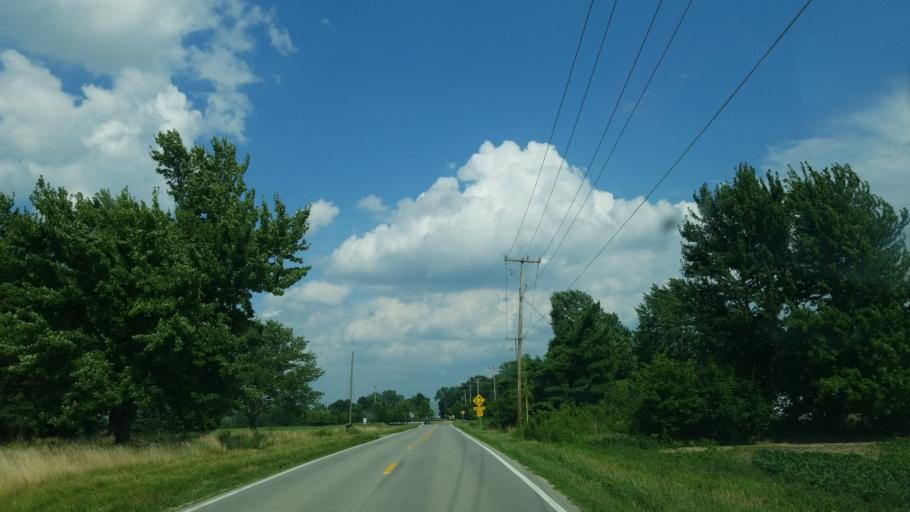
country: US
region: Ohio
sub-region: Delaware County
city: Powell
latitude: 40.2166
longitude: -83.1007
